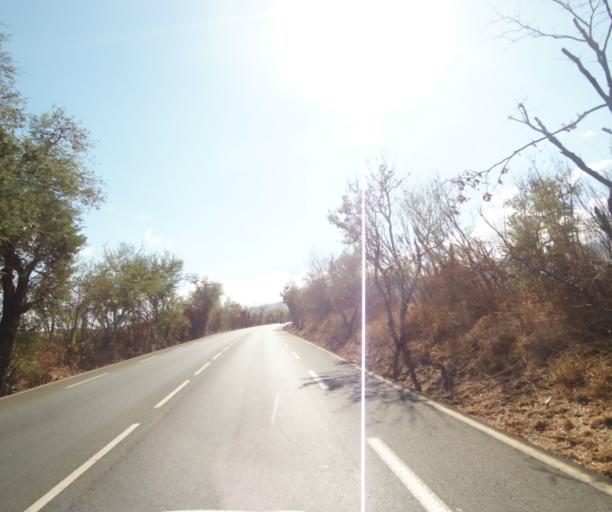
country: RE
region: Reunion
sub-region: Reunion
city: Saint-Paul
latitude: -20.9835
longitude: 55.3027
